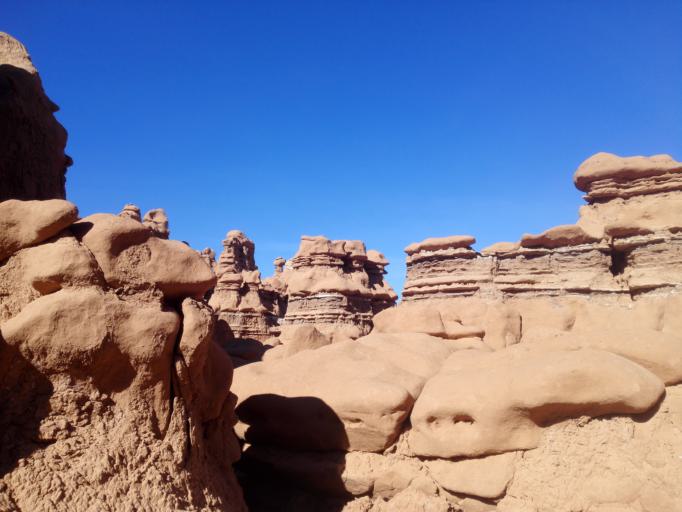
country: US
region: Utah
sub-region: Emery County
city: Ferron
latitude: 38.5581
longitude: -110.6983
